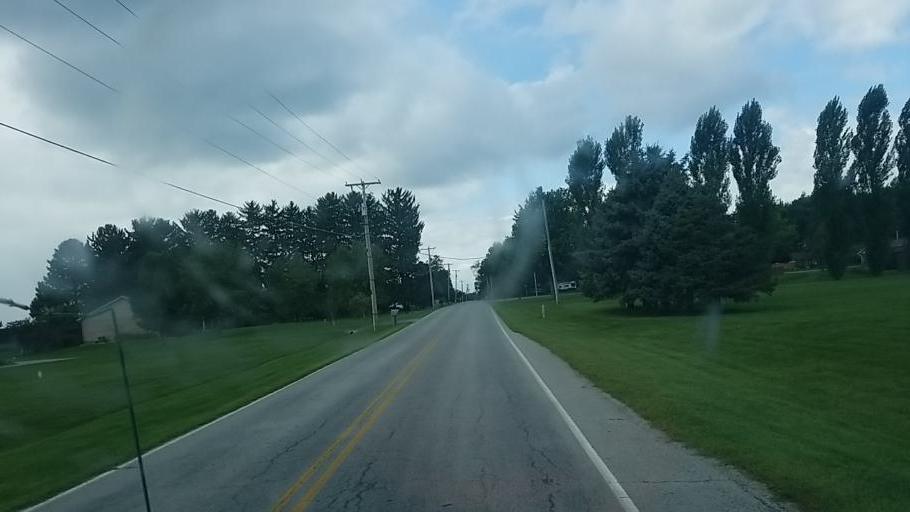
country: US
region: Ohio
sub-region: Clark County
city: Springfield
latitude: 39.8776
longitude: -83.7726
